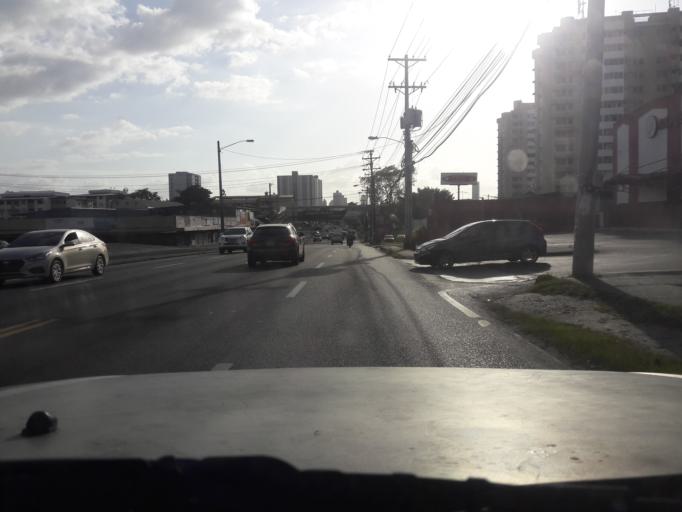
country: PA
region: Panama
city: San Miguelito
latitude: 9.0225
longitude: -79.4889
